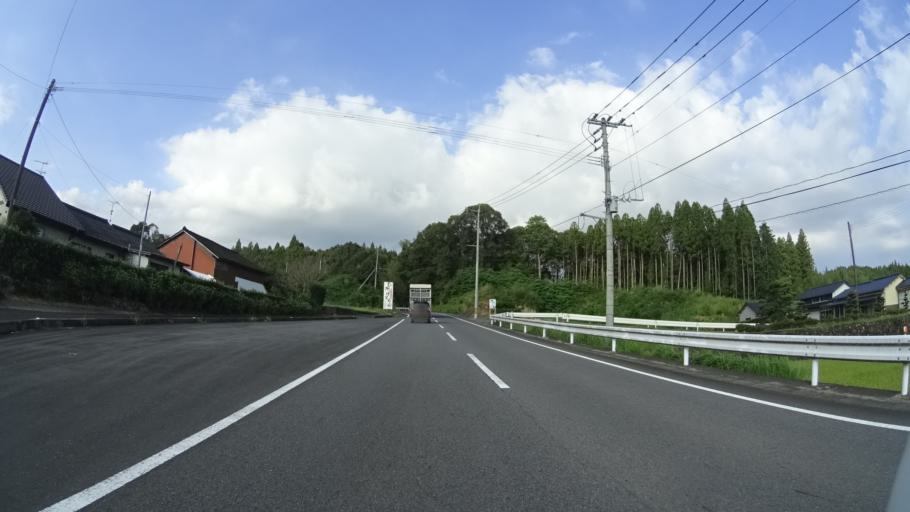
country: JP
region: Kagoshima
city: Okuchi-shinohara
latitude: 32.0238
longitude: 130.5945
